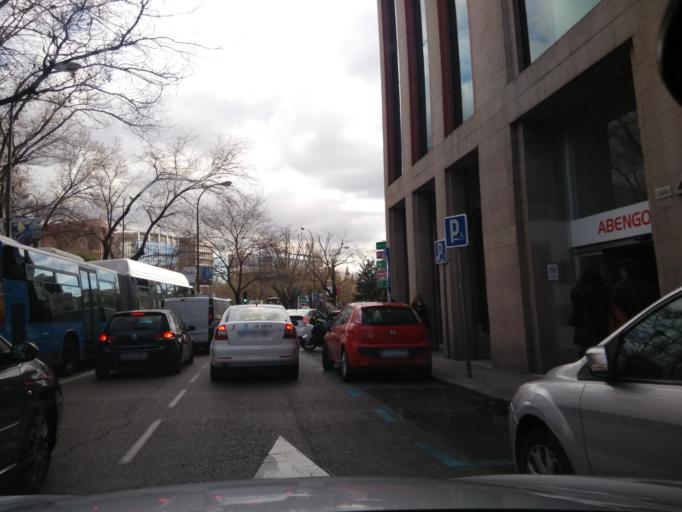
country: ES
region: Madrid
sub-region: Provincia de Madrid
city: Salamanca
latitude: 40.4357
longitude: -3.6896
